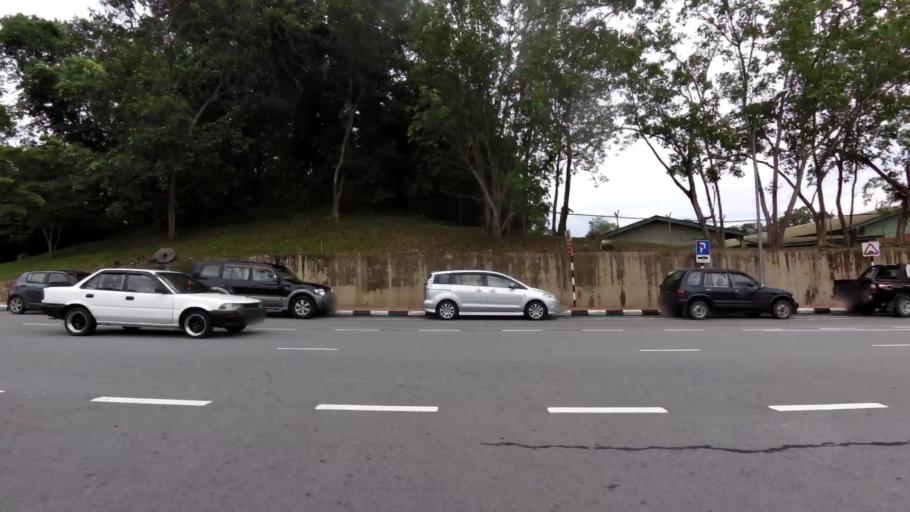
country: BN
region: Brunei and Muara
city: Bandar Seri Begawan
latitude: 4.8935
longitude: 114.9308
